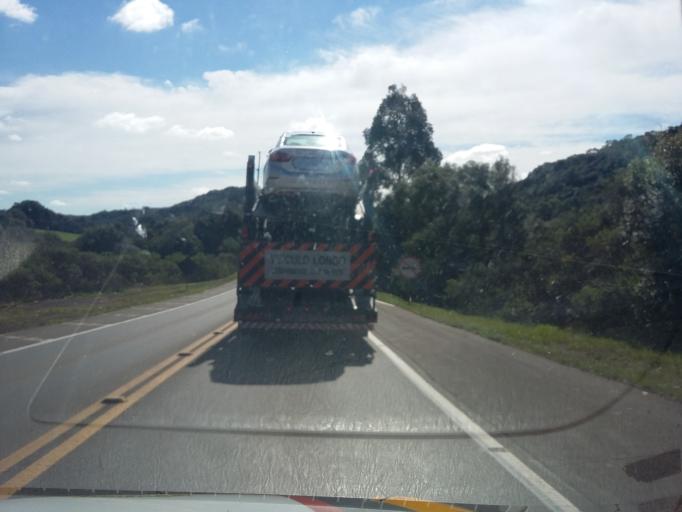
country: BR
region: Rio Grande do Sul
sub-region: Vacaria
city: Vacaria
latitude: -28.5864
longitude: -51.0281
